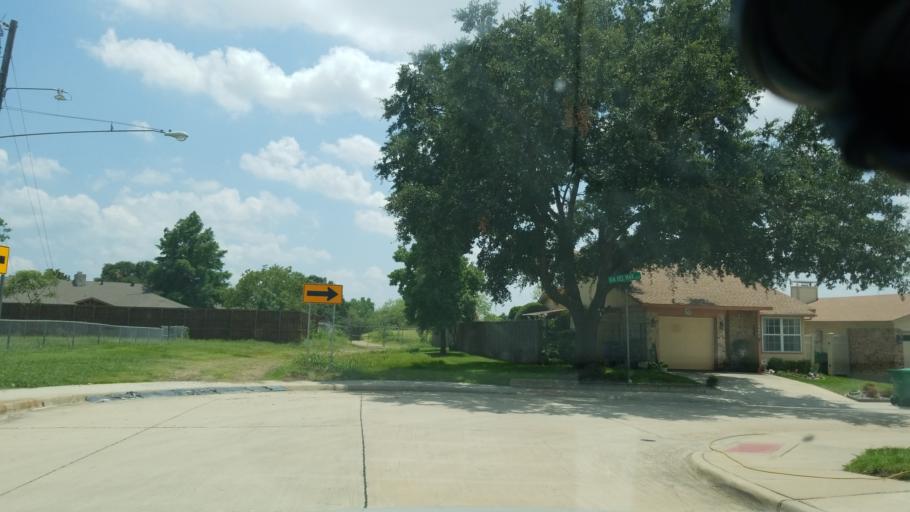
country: US
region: Texas
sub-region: Dallas County
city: Carrollton
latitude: 32.9660
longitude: -96.8641
